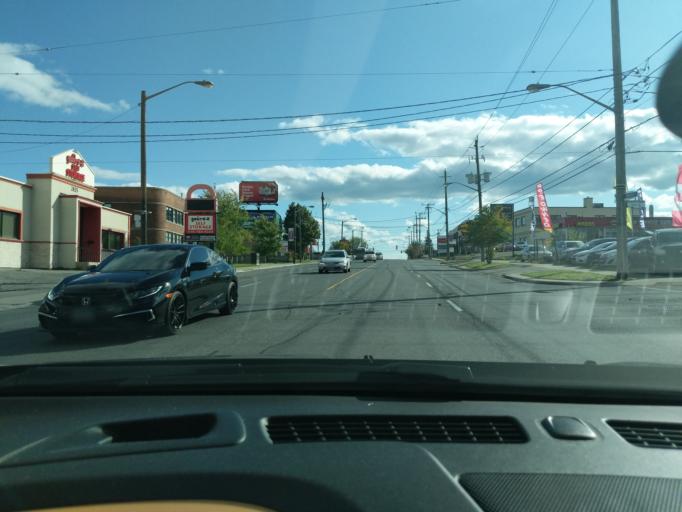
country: CA
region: Ontario
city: Toronto
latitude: 43.7059
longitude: -79.4530
